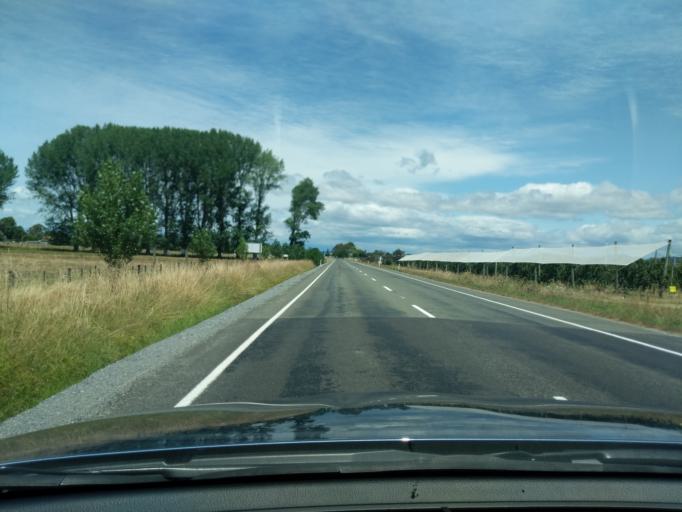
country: NZ
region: Tasman
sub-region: Tasman District
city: Motueka
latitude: -41.0713
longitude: 172.9957
